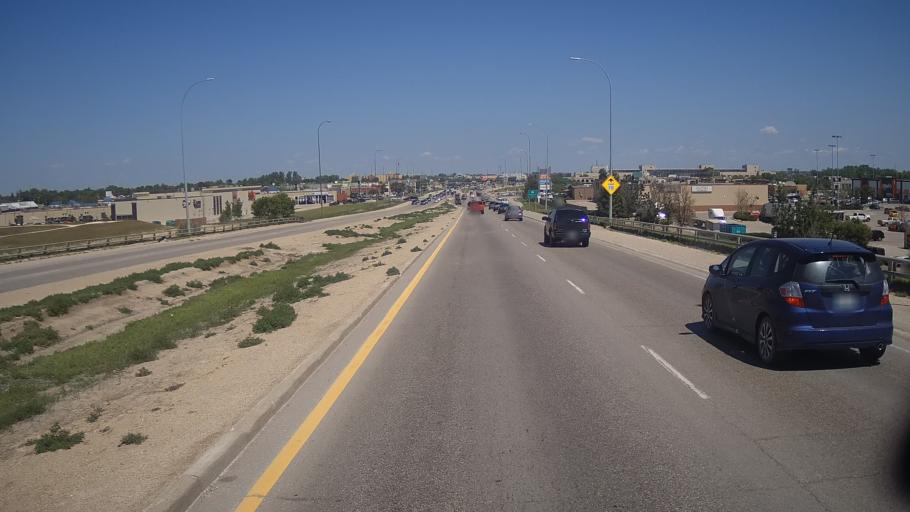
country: CA
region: Manitoba
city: Winnipeg
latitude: 49.8948
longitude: -97.0705
